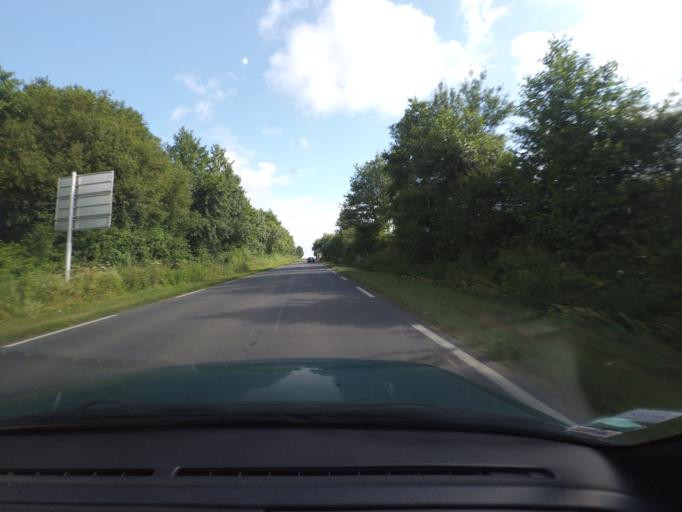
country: FR
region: Pays de la Loire
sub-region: Departement de la Loire-Atlantique
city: Mouzillon
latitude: 47.1177
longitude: -1.2827
